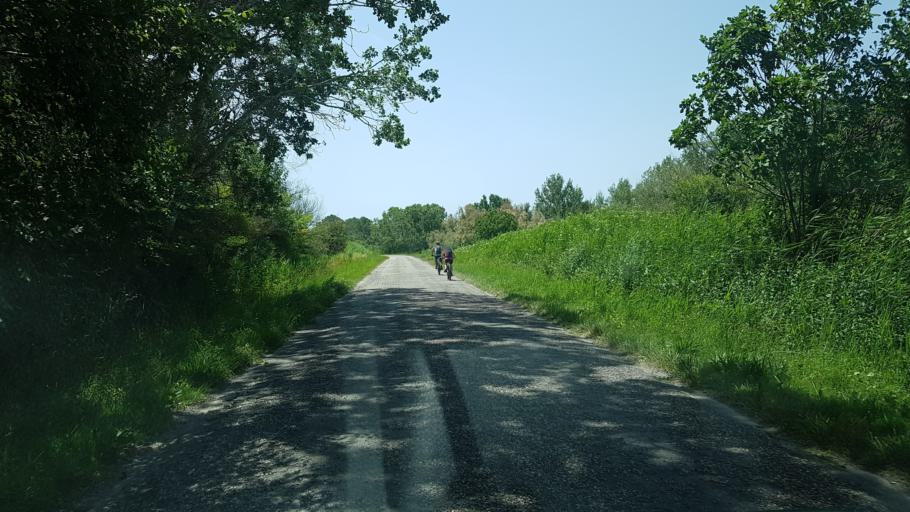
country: FR
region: Provence-Alpes-Cote d'Azur
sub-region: Departement des Bouches-du-Rhone
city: Arles
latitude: 43.5623
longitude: 4.6239
